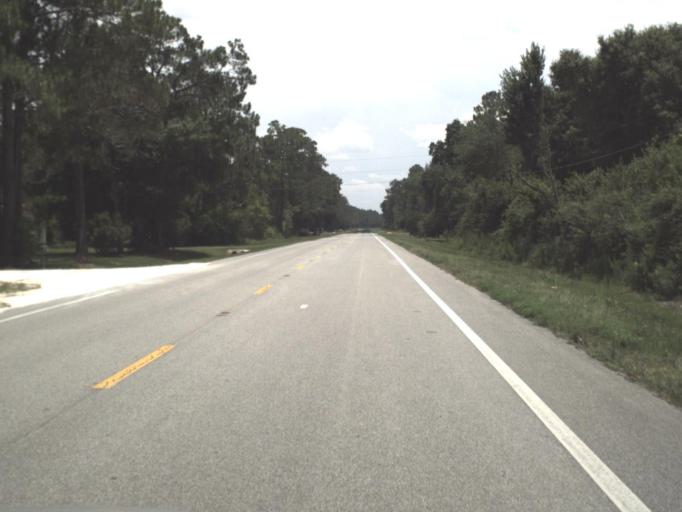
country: US
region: Florida
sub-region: Bradford County
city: Starke
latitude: 29.9943
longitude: -82.1312
